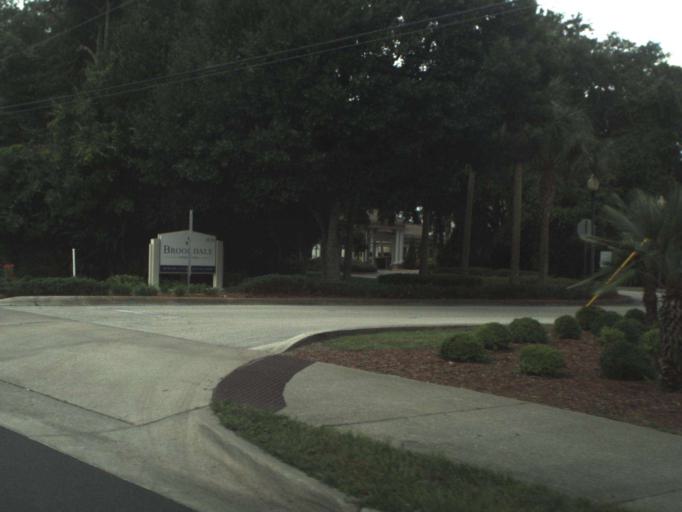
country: US
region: Florida
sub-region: Volusia County
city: Port Orange
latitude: 29.1137
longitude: -81.0251
